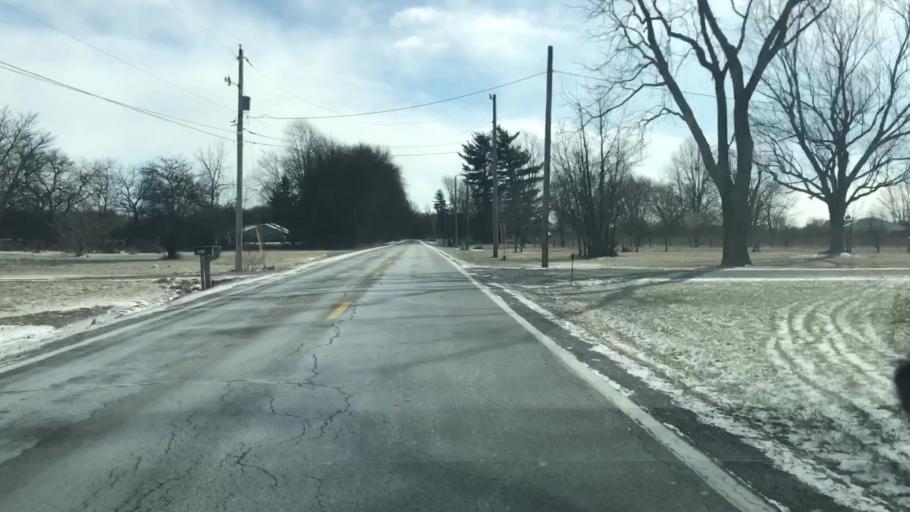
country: US
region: Ohio
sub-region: Franklin County
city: Hilliard
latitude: 40.0229
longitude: -83.2216
